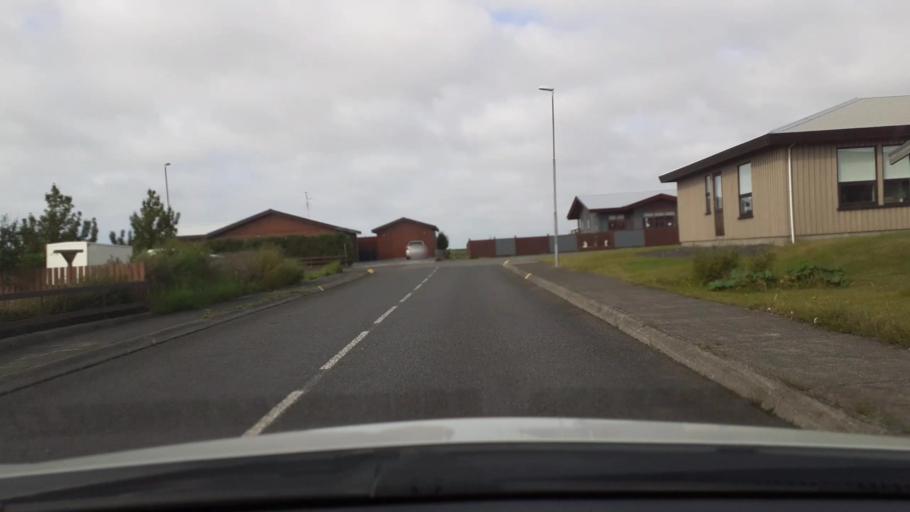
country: IS
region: South
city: THorlakshoefn
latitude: 63.8576
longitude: -21.3957
